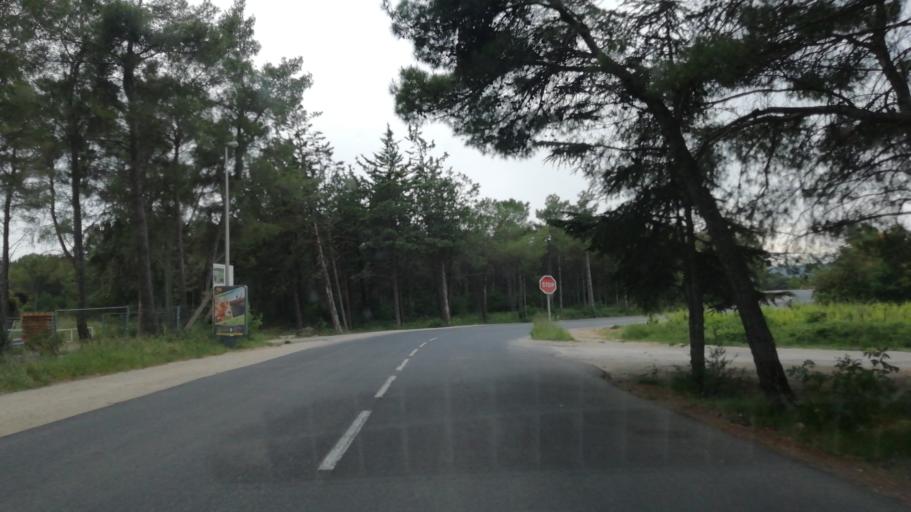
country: FR
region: Languedoc-Roussillon
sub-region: Departement de l'Herault
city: Saint-Mathieu-de-Treviers
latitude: 43.7611
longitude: 3.8696
